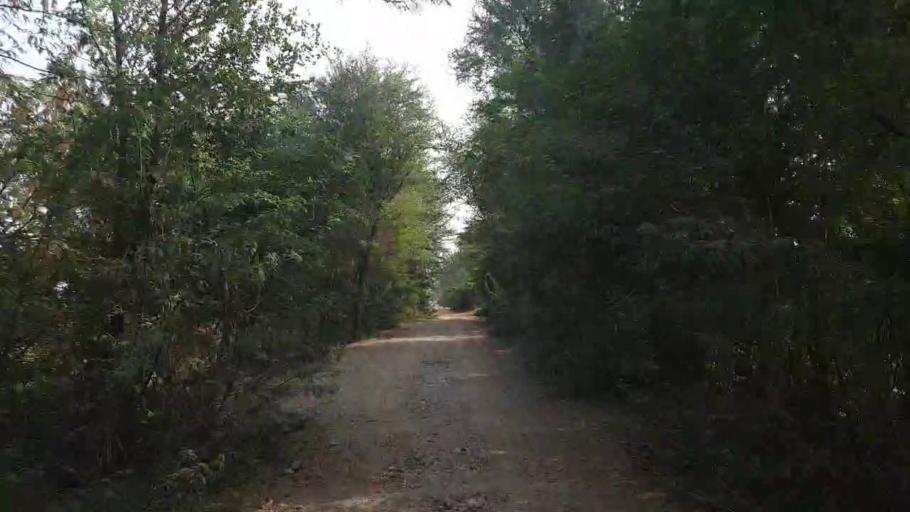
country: PK
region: Sindh
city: Sann
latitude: 26.0560
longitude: 68.1126
